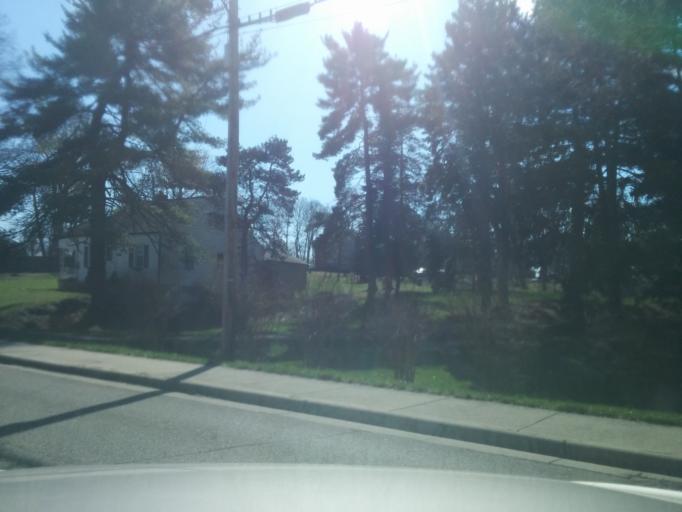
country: US
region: Ohio
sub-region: Hamilton County
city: Monfort Heights
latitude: 39.1983
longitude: -84.5920
